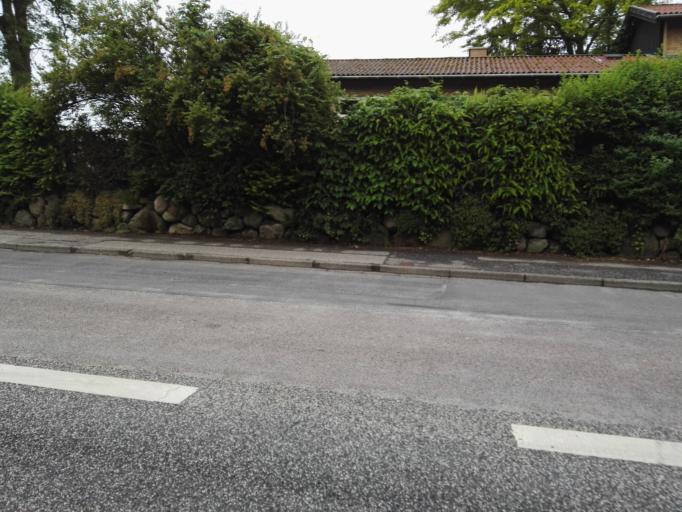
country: DK
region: Capital Region
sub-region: Ballerup Kommune
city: Ballerup
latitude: 55.7551
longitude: 12.3729
